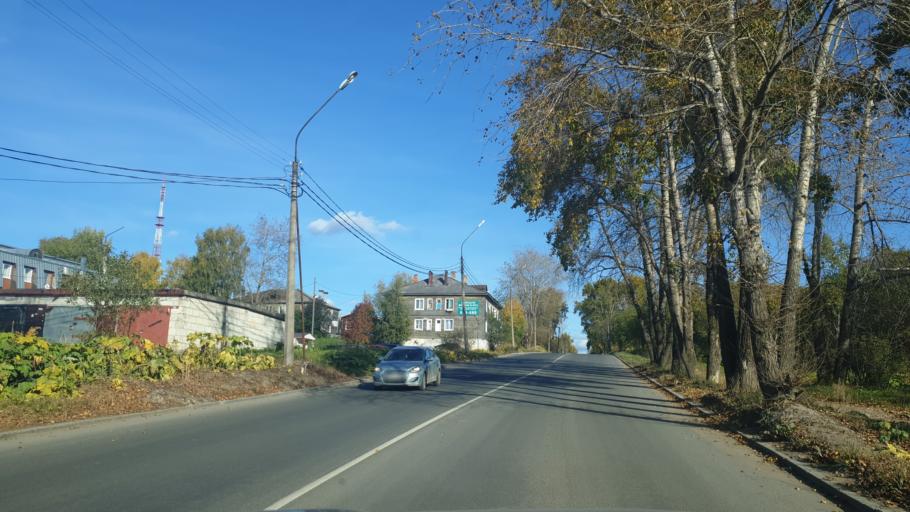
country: RU
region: Komi Republic
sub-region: Syktyvdinskiy Rayon
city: Syktyvkar
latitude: 61.6850
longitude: 50.7982
